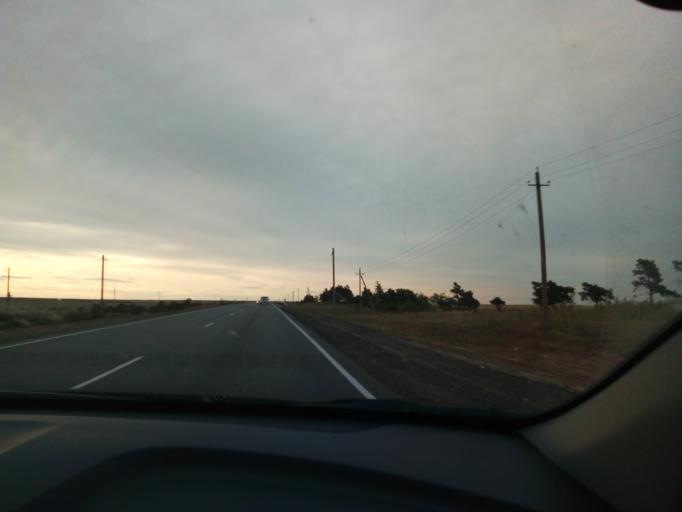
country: RU
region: Volgograd
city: Primorsk
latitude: 49.2520
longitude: 44.8880
